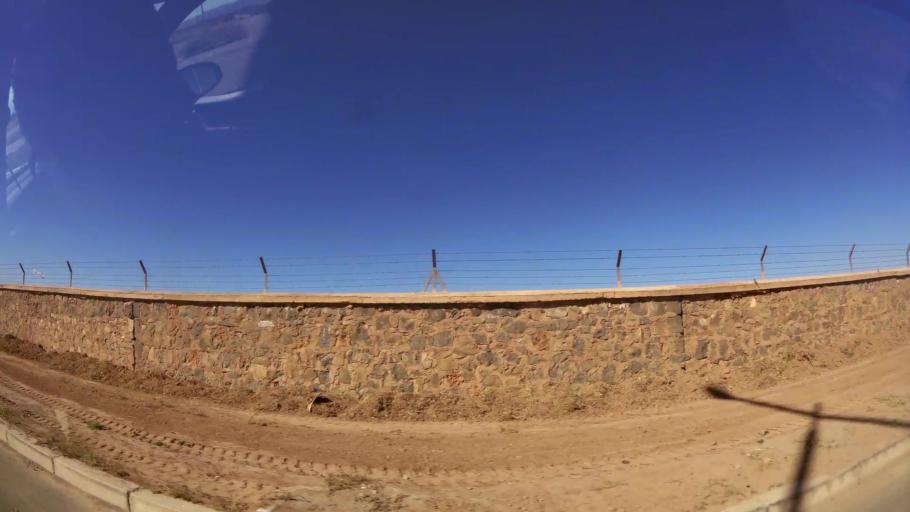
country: MA
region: Oriental
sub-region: Oujda-Angad
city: Oujda
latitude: 34.7753
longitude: -1.9318
